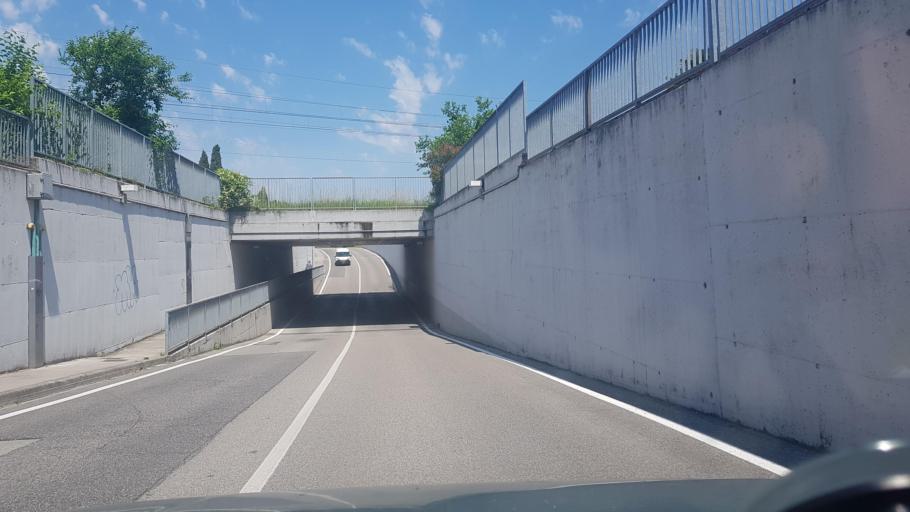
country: IT
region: Friuli Venezia Giulia
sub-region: Provincia di Gorizia
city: Pieris
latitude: 45.8143
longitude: 13.4451
